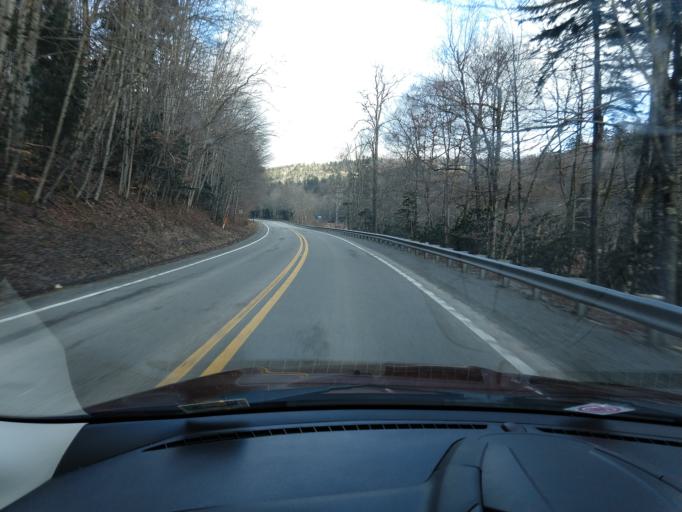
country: US
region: West Virginia
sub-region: Randolph County
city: Elkins
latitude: 38.6285
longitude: -79.8723
